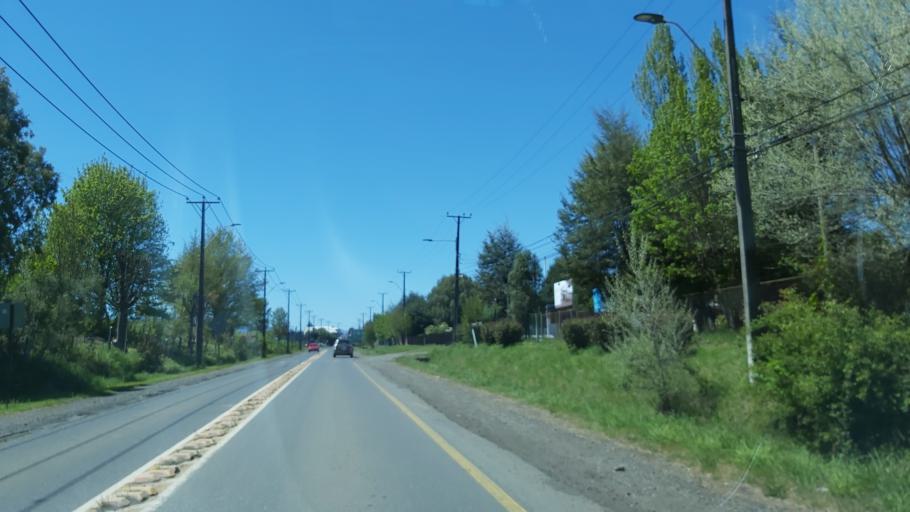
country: CL
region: Araucania
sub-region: Provincia de Cautin
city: Vilcun
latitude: -38.4348
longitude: -71.9018
